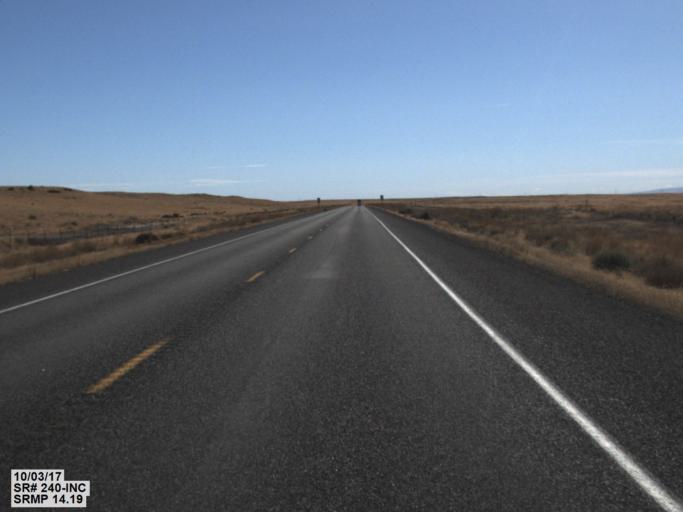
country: US
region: Washington
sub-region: Benton County
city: Benton City
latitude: 46.4515
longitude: -119.5083
